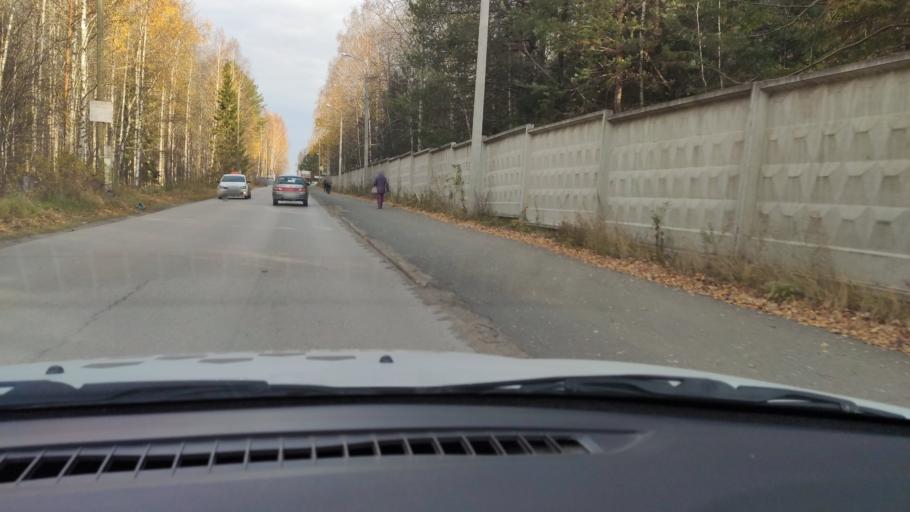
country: RU
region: Perm
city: Kondratovo
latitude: 58.0627
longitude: 56.1252
